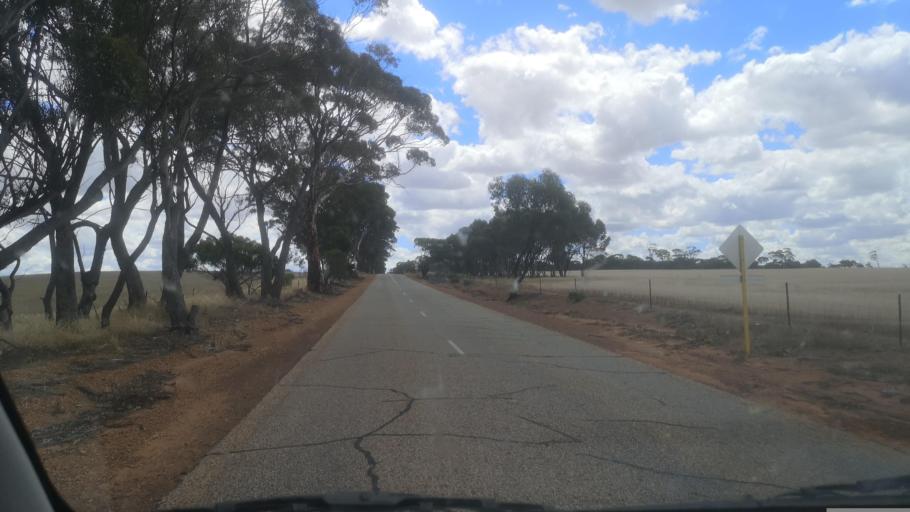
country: AU
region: Western Australia
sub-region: Beverley
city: Beverley
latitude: -31.9900
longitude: 117.1196
